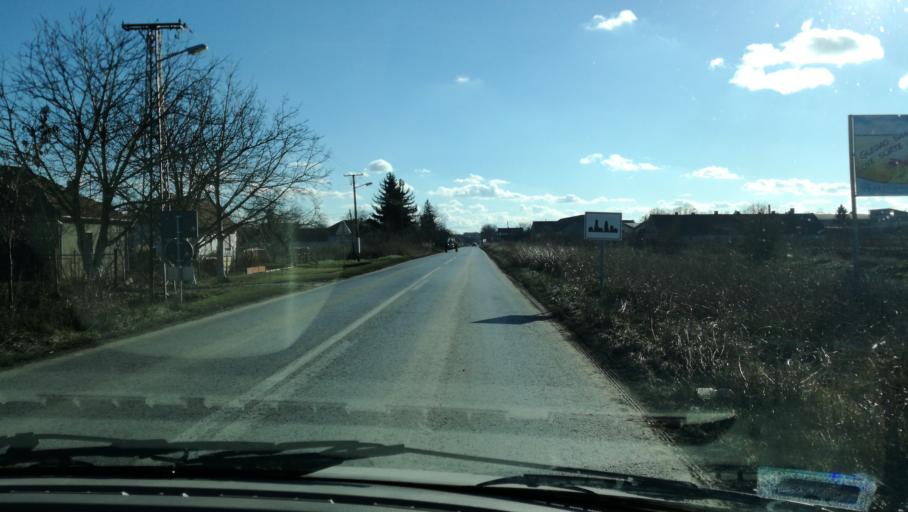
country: RS
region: Autonomna Pokrajina Vojvodina
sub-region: Severnobanatski Okrug
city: Coka
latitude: 45.9475
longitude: 20.1404
